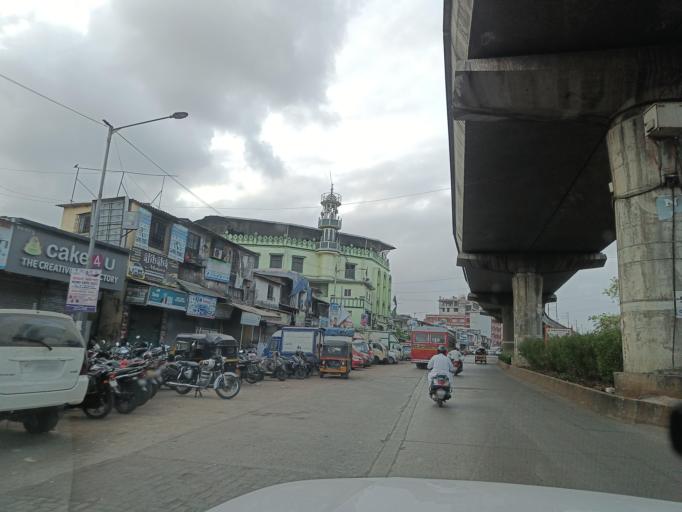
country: IN
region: Maharashtra
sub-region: Mumbai Suburban
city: Powai
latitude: 19.1017
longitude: 72.8905
